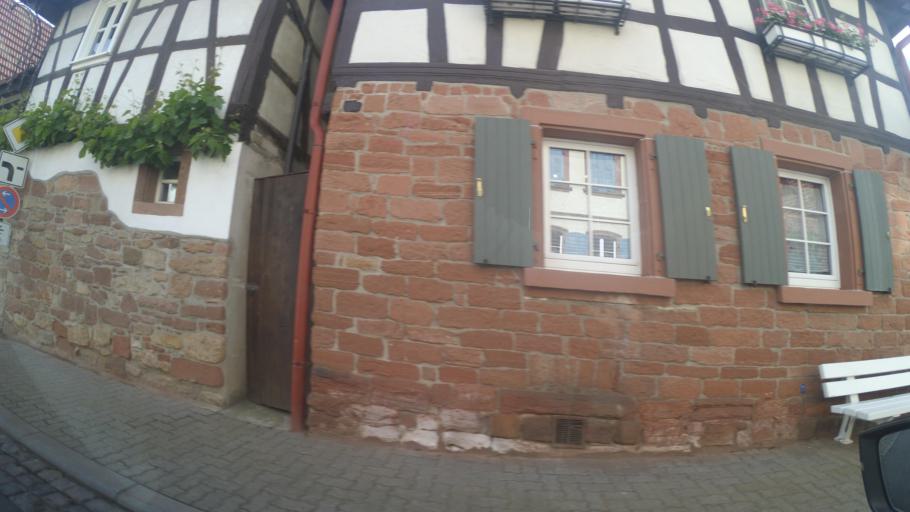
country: DE
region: Rheinland-Pfalz
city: Heuchelheim-Klingen
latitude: 49.1473
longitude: 8.0540
